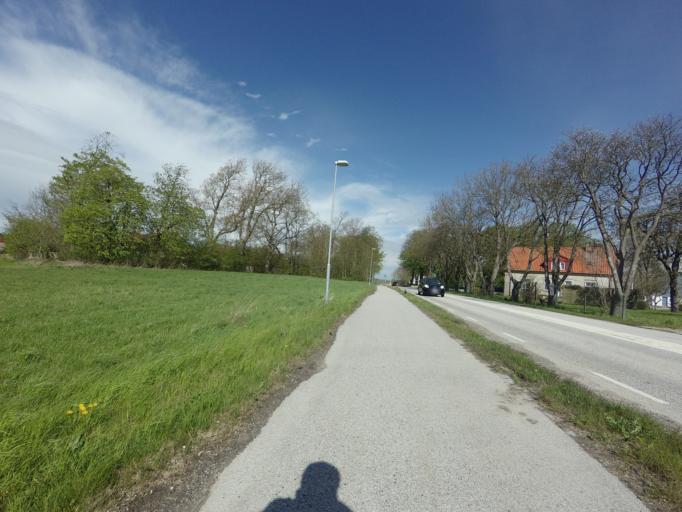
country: SE
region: Skane
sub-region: Malmo
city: Tygelsjo
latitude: 55.5010
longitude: 12.9965
